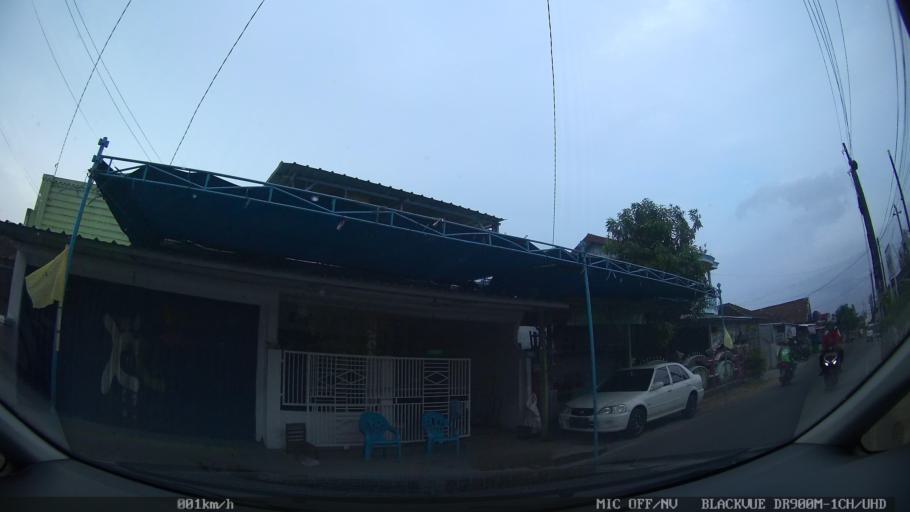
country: ID
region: Lampung
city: Kedaton
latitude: -5.3993
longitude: 105.2675
